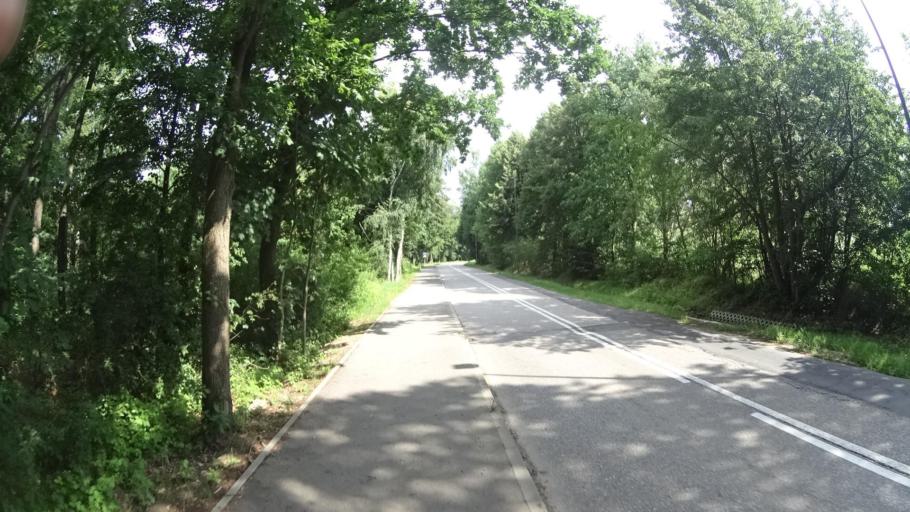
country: PL
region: Masovian Voivodeship
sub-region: Powiat pruszkowski
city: Nadarzyn
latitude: 52.0406
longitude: 20.7823
